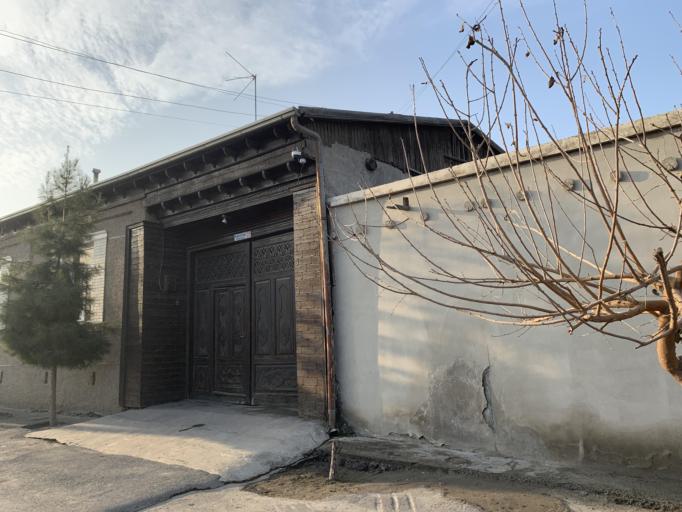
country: UZ
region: Fergana
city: Qo`qon
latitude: 40.5395
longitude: 70.9311
